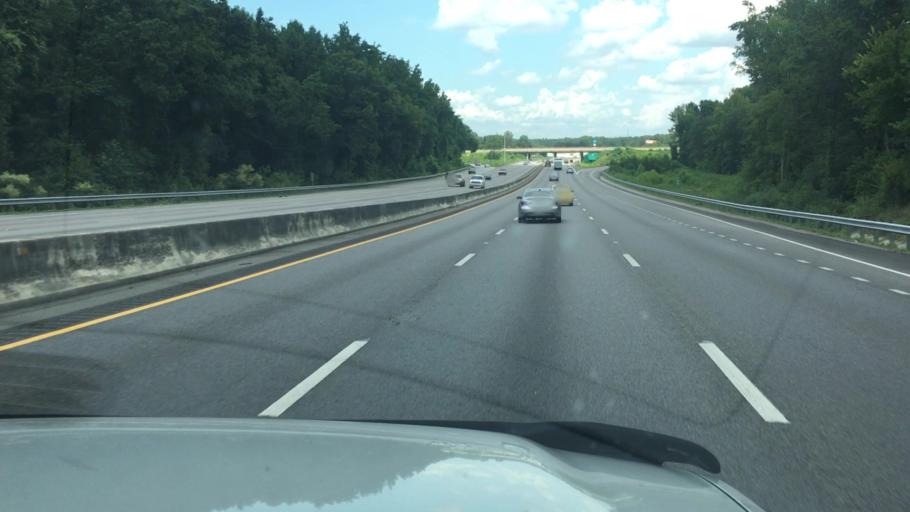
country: US
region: South Carolina
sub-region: Richland County
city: Columbia
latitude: 34.0589
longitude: -81.0508
